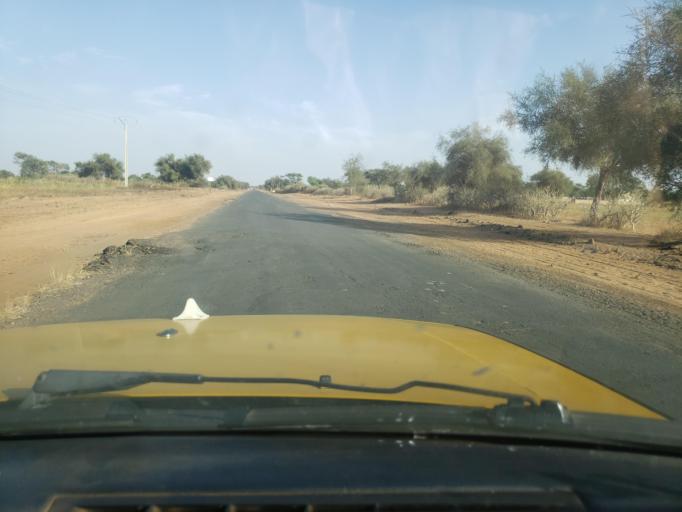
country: SN
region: Louga
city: Louga
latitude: 15.5022
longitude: -15.9438
